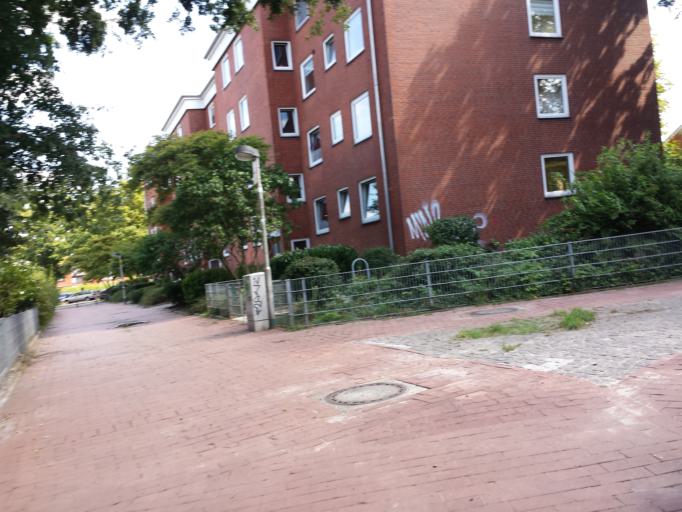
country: DE
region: Bremen
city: Bremen
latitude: 53.0420
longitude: 8.8197
